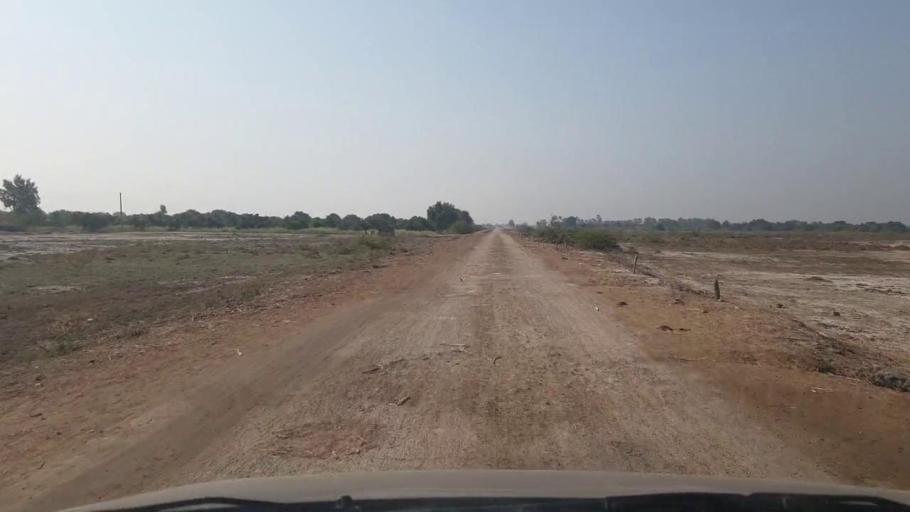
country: PK
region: Sindh
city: Mirwah Gorchani
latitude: 25.2721
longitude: 69.1188
